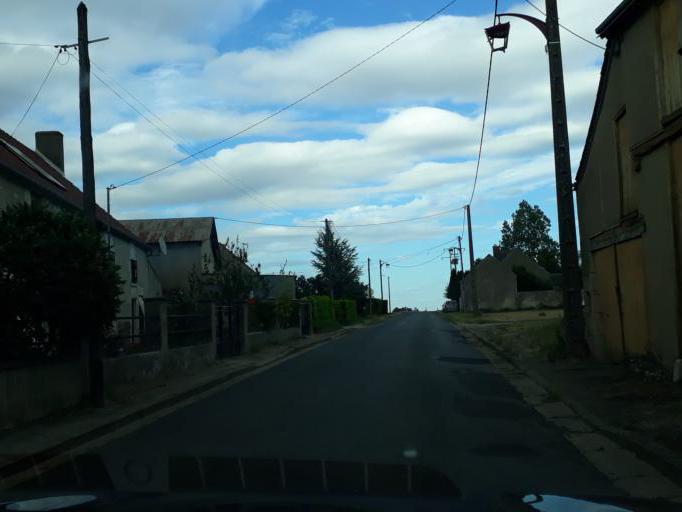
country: FR
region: Centre
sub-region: Departement du Loir-et-Cher
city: Mer
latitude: 47.8022
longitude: 1.4951
